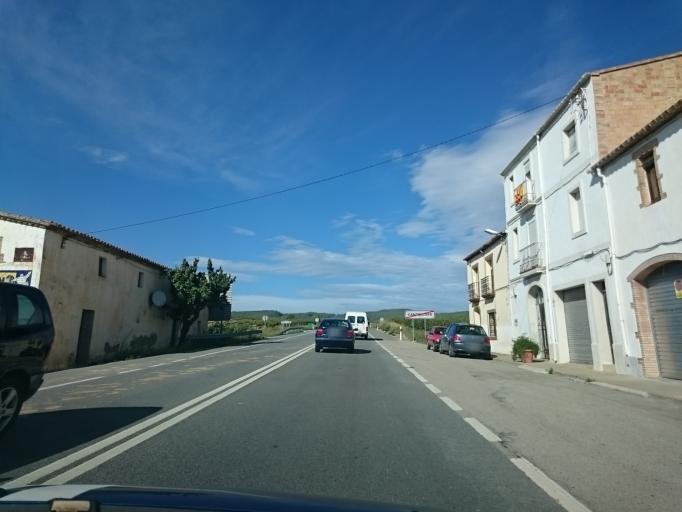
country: ES
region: Catalonia
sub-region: Provincia de Barcelona
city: Avinyonet del Penedes
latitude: 41.3713
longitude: 1.8044
